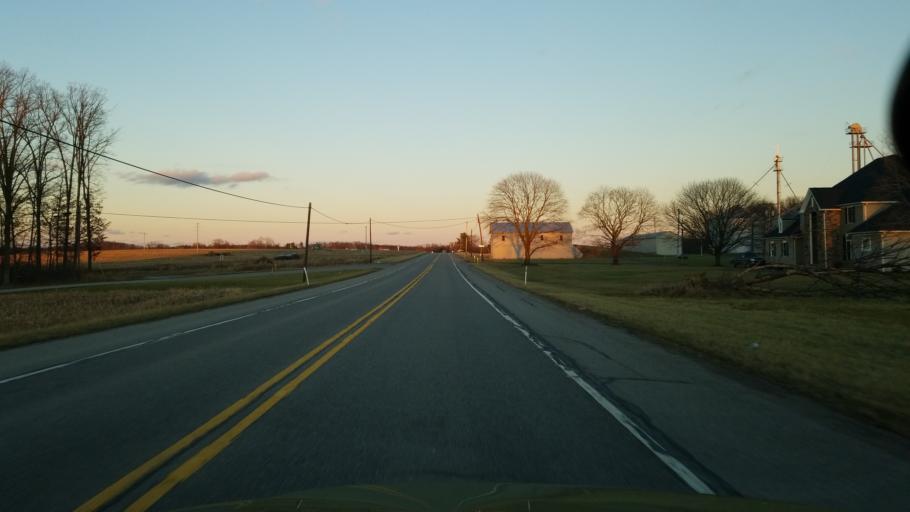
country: US
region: Pennsylvania
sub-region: Jefferson County
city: Punxsutawney
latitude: 40.8496
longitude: -79.0336
